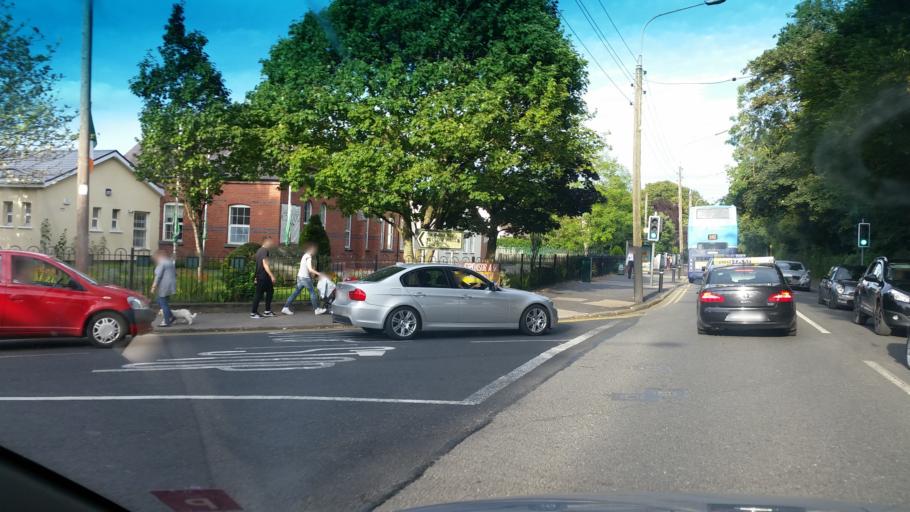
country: IE
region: Leinster
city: Malahide
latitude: 53.4492
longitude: -6.1638
